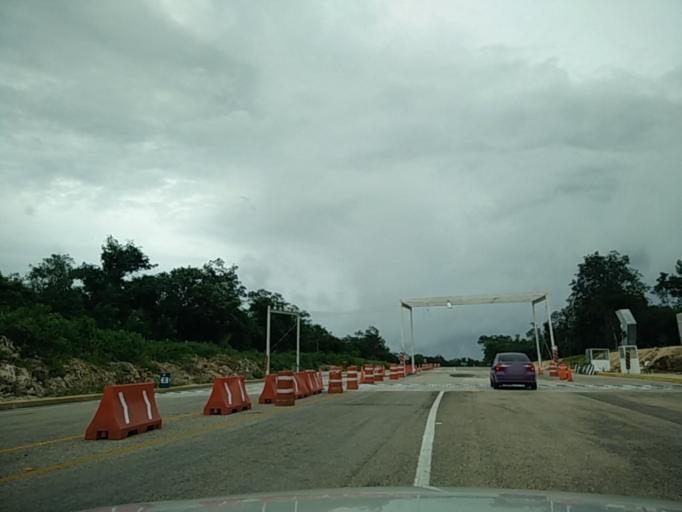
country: MX
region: Quintana Roo
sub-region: Lazaro Cardenas
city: El Tintal
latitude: 20.8896
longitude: -87.4341
